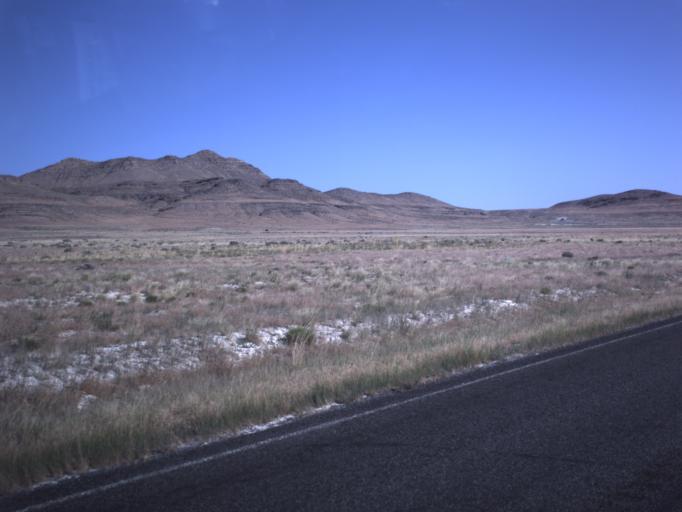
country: US
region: Utah
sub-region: Beaver County
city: Milford
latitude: 38.8502
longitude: -112.8423
